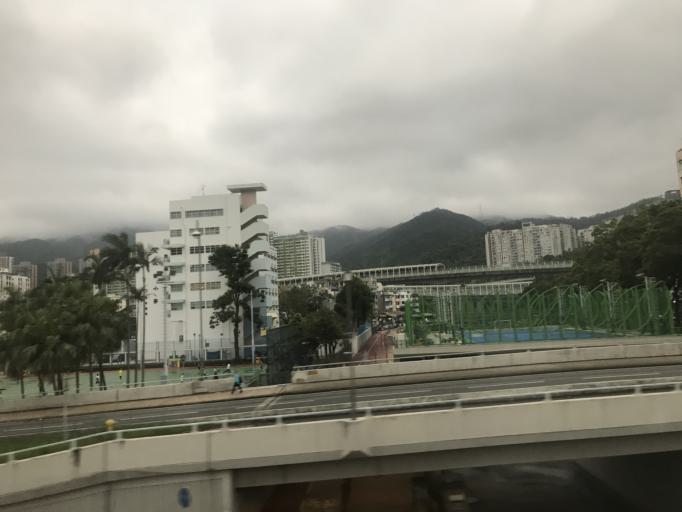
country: HK
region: Sha Tin
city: Sha Tin
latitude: 22.3748
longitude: 114.1807
